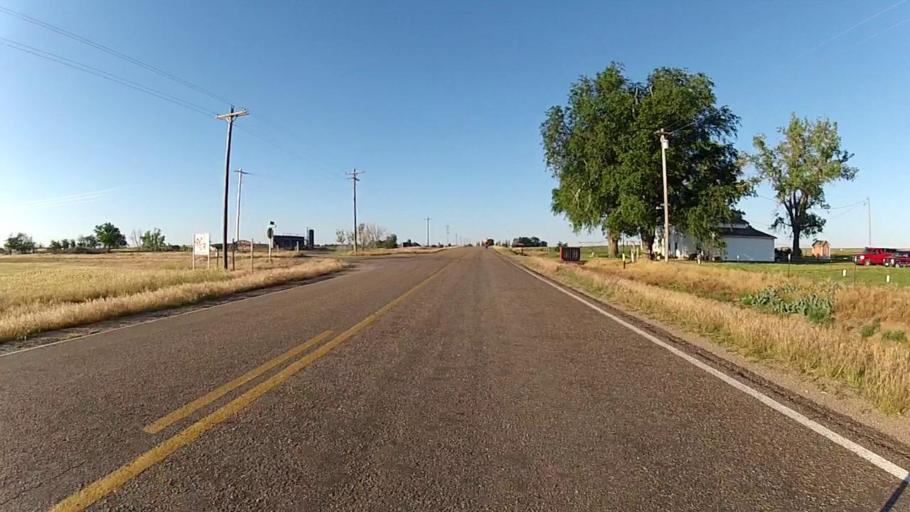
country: US
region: Kansas
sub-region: Ford County
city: Dodge City
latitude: 37.7027
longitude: -99.9064
